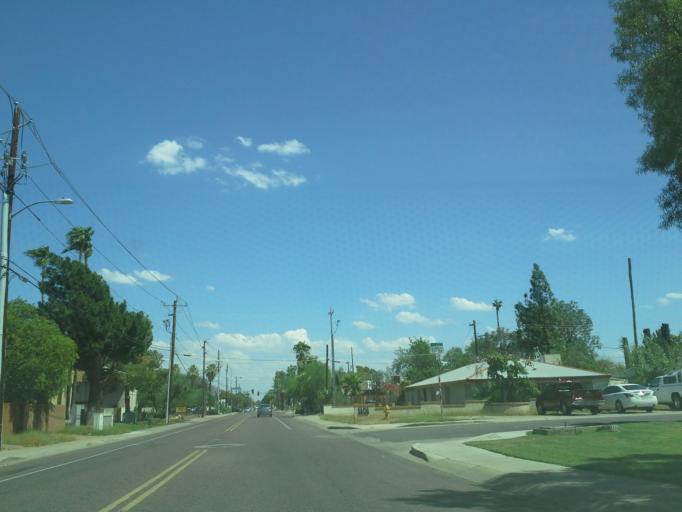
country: US
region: Arizona
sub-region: Maricopa County
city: Phoenix
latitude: 33.5056
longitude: -112.0588
